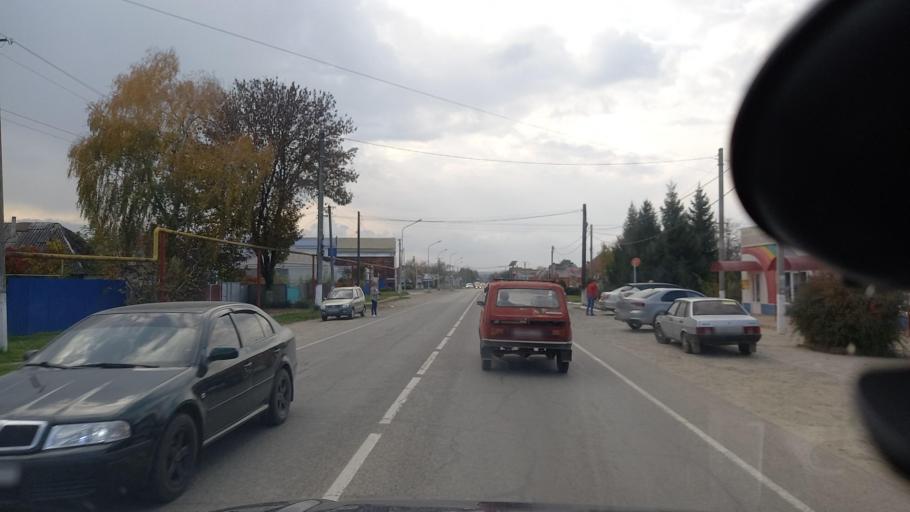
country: RU
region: Krasnodarskiy
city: Mostovskoy
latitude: 44.4075
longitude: 40.7981
